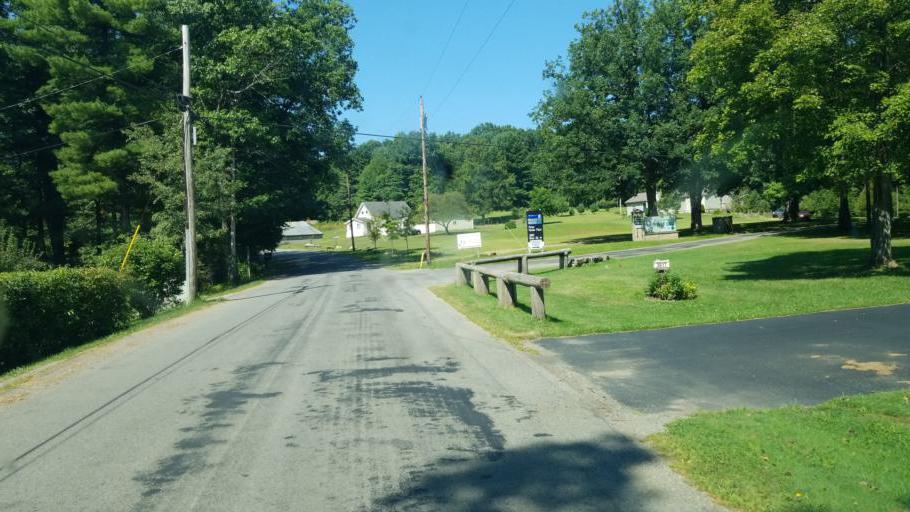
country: US
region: Pennsylvania
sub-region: Clarion County
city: Clarion
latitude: 41.1730
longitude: -79.4275
